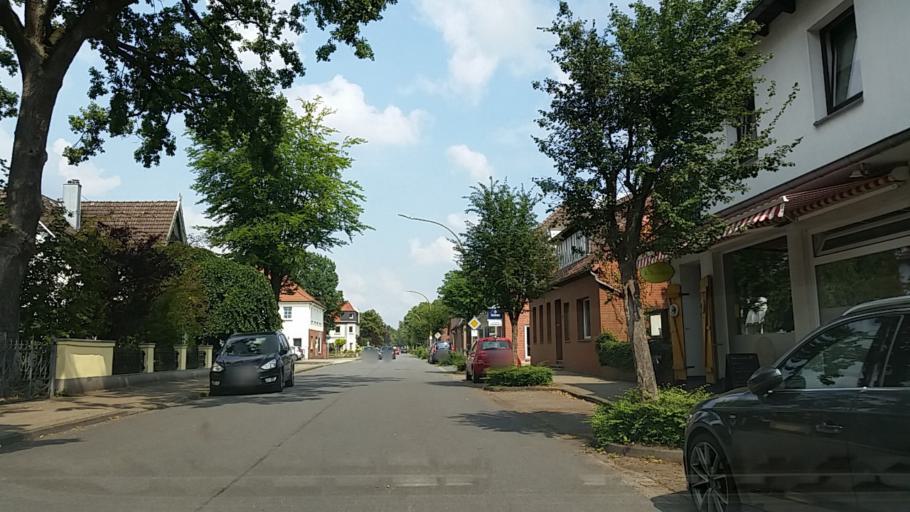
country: DE
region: Lower Saxony
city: Schneverdingen
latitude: 53.1204
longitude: 9.7880
